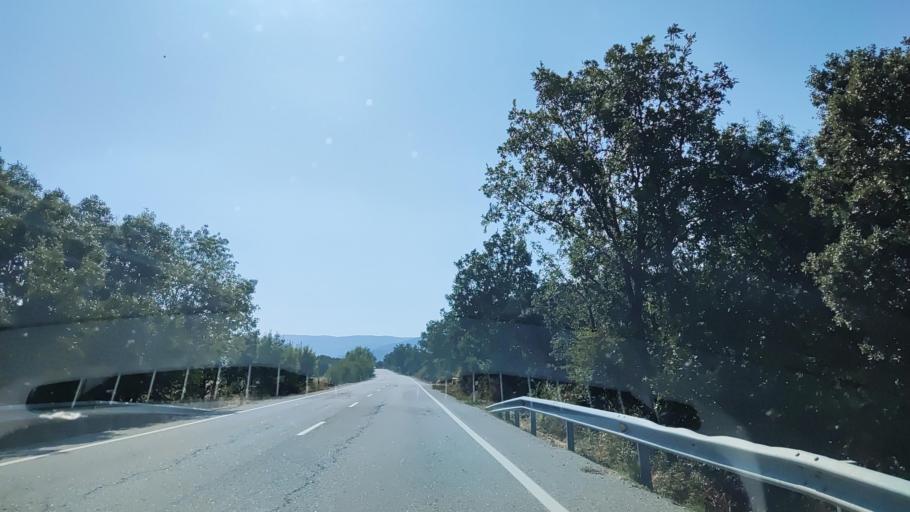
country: ES
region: Madrid
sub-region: Provincia de Madrid
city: Canencia
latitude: 40.9468
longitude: -3.7468
